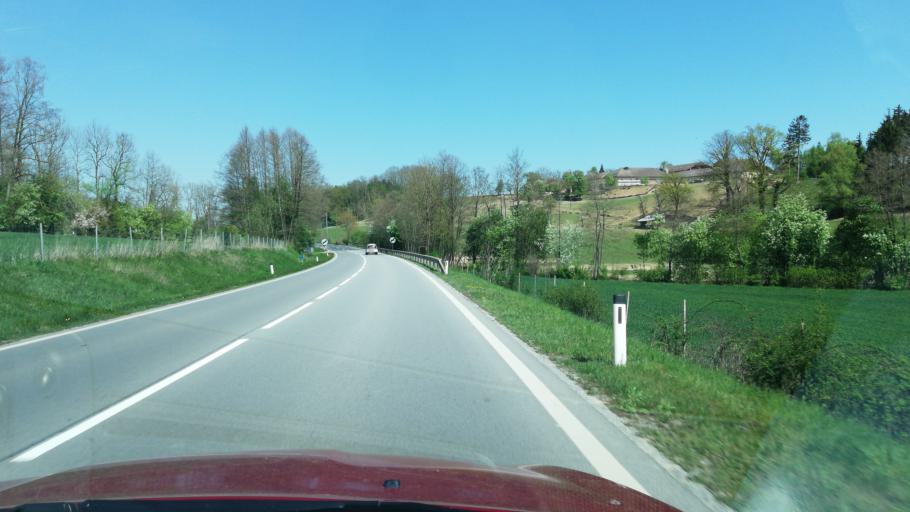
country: AT
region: Upper Austria
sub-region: Wels-Land
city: Thalheim bei Wels
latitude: 48.1284
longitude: 14.0520
